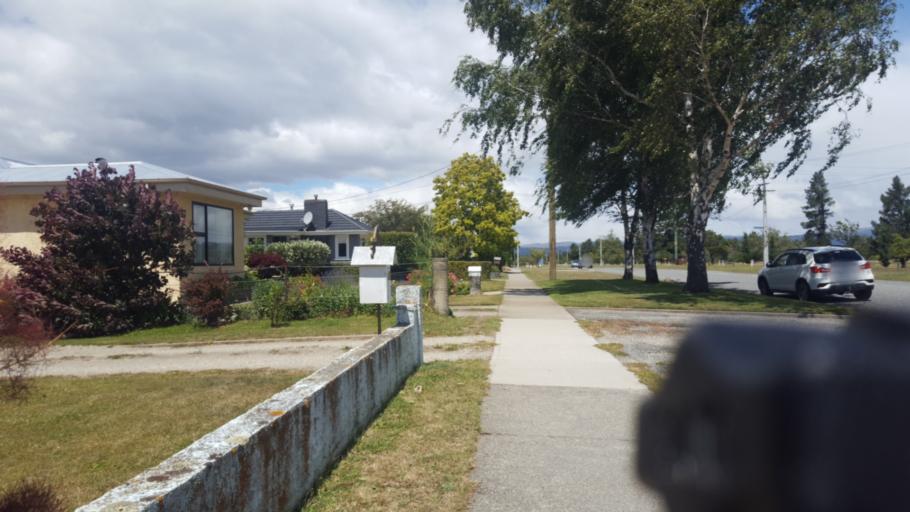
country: NZ
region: Otago
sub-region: Queenstown-Lakes District
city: Wanaka
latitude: -45.1923
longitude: 169.3239
